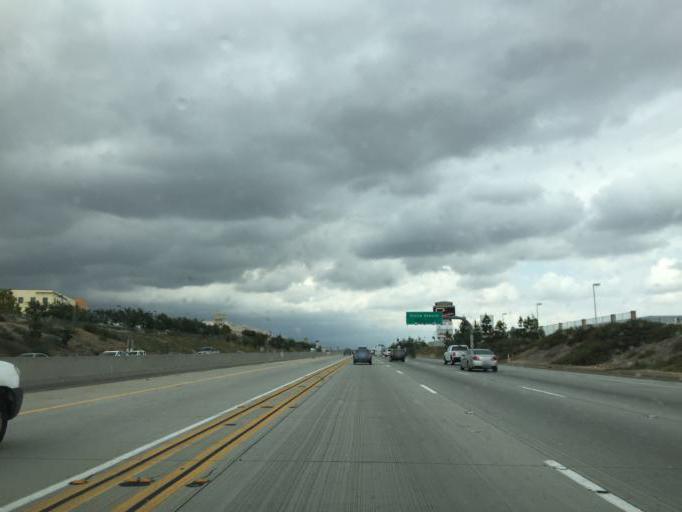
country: US
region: California
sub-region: San Bernardino County
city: Fontana
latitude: 34.1363
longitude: -117.4475
